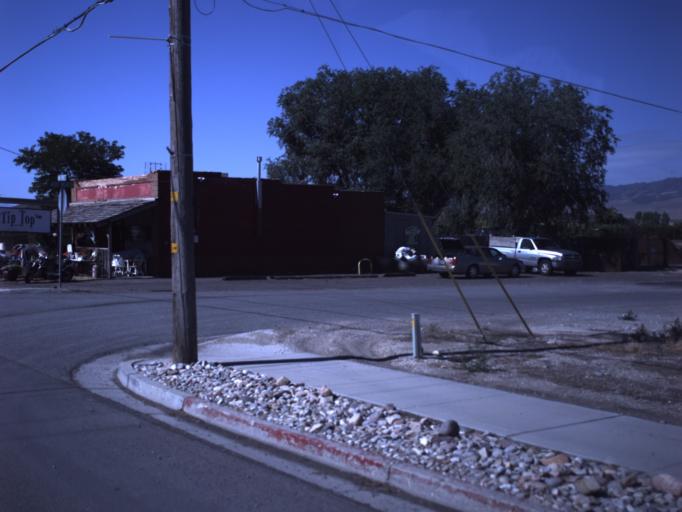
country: US
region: Utah
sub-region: Sanpete County
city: Centerfield
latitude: 39.1344
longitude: -111.8191
